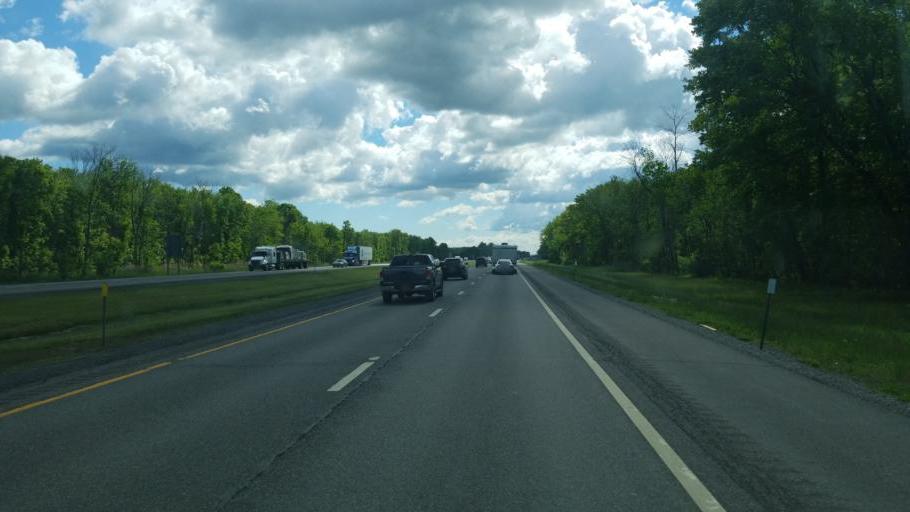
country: US
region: New York
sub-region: Onondaga County
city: Minoa
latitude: 43.0940
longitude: -75.9916
